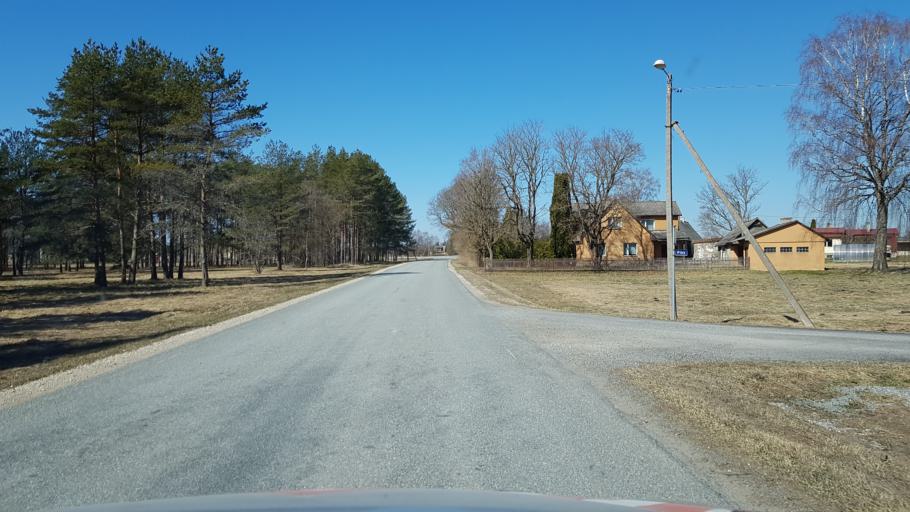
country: EE
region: Laeaene-Virumaa
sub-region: Rakke vald
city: Rakke
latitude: 59.0466
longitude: 26.3973
